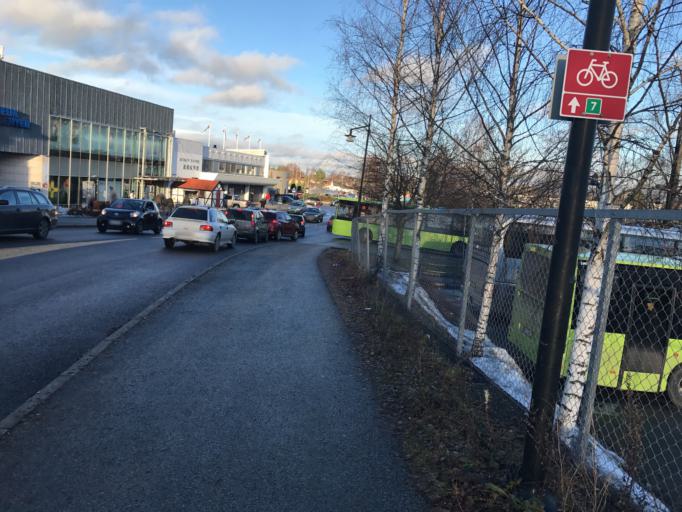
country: NO
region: Akershus
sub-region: Ullensaker
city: Jessheim
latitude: 60.1417
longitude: 11.1754
